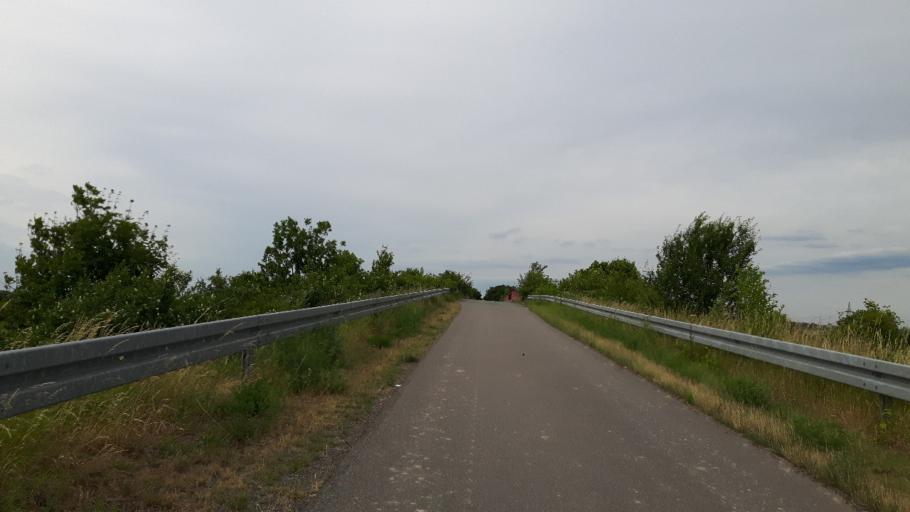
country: DE
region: Saxony
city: Rackwitz
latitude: 51.4131
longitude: 12.3192
